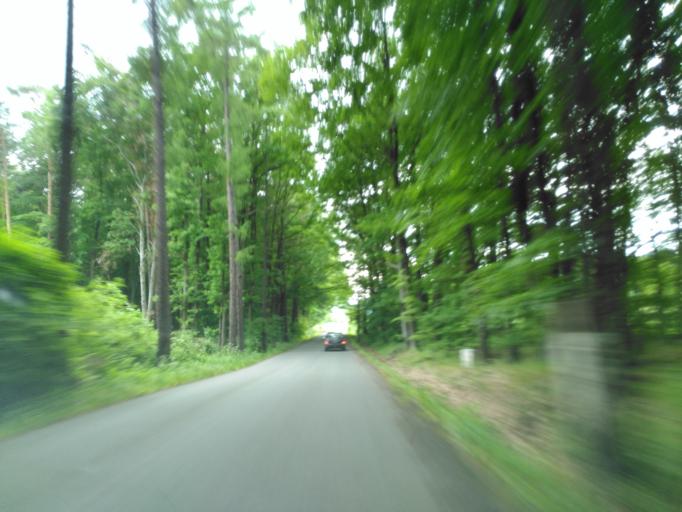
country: CZ
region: Central Bohemia
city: Zebrak
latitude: 49.9407
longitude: 13.8934
